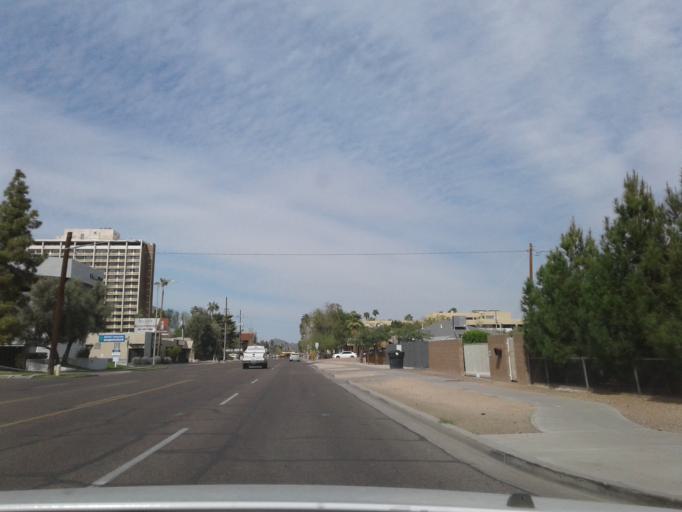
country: US
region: Arizona
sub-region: Maricopa County
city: Phoenix
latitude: 33.4909
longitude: -112.0694
